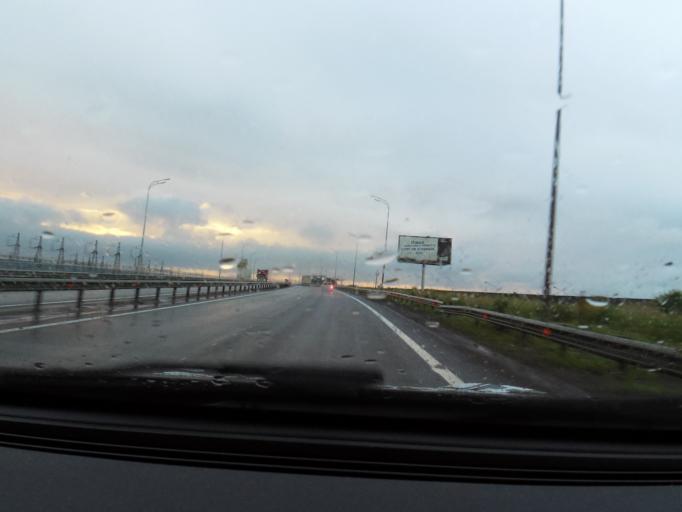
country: RU
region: Tatarstan
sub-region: Tukayevskiy Rayon
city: Naberezhnyye Chelny
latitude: 55.6903
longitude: 52.2831
